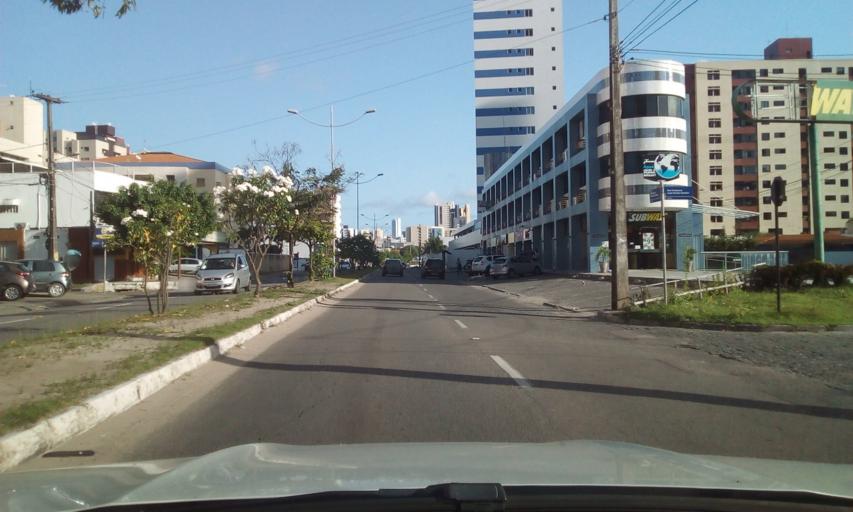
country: BR
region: Paraiba
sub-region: Joao Pessoa
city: Joao Pessoa
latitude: -7.0896
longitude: -34.8384
